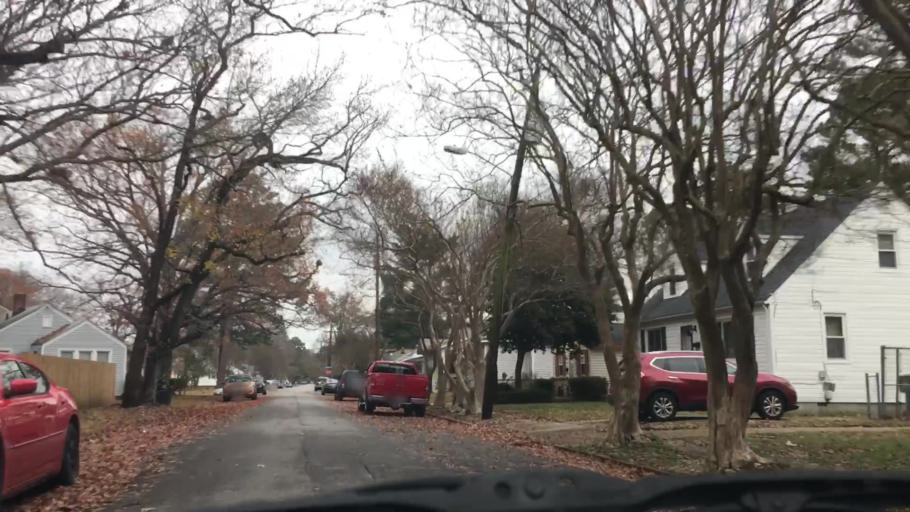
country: US
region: Virginia
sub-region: City of Norfolk
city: Norfolk
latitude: 36.8762
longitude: -76.2465
